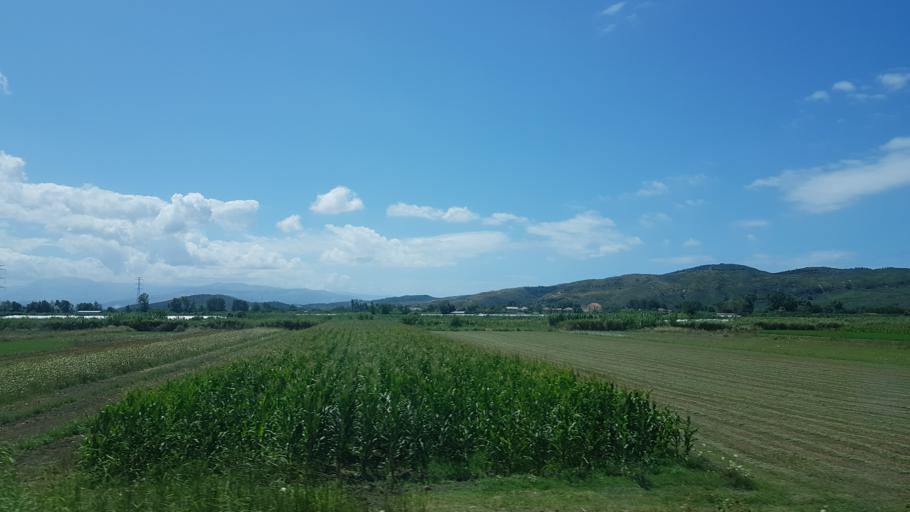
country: AL
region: Fier
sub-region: Rrethi i Fierit
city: Frakulla e Madhe
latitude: 40.6058
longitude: 19.5449
